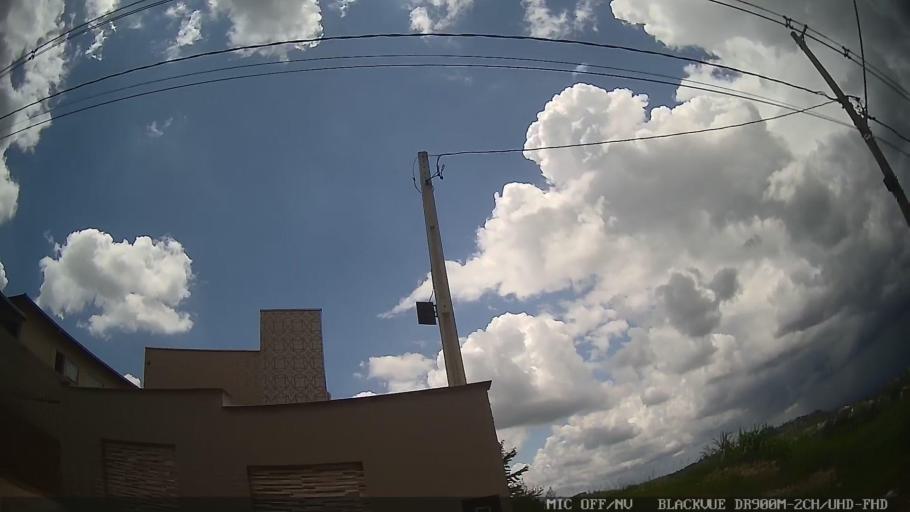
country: BR
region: Sao Paulo
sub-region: Serra Negra
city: Serra Negra
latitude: -22.6018
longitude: -46.7145
